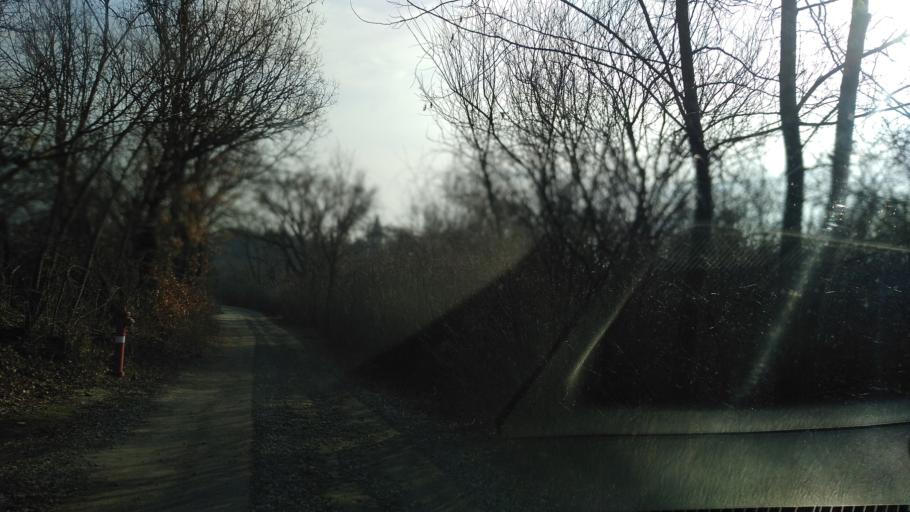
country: HU
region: Pest
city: Szentendre
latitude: 47.6958
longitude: 19.0499
